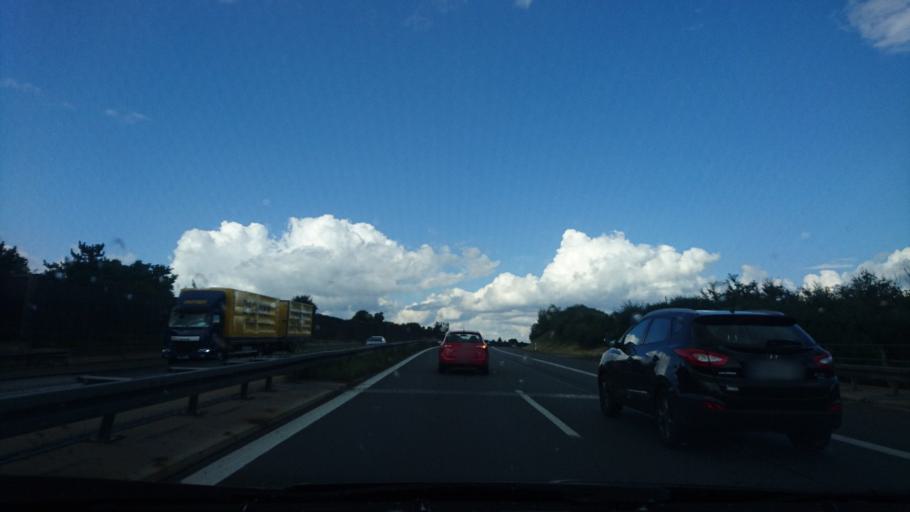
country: DE
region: Saxony
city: Neuensalz
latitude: 50.4881
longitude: 12.1882
